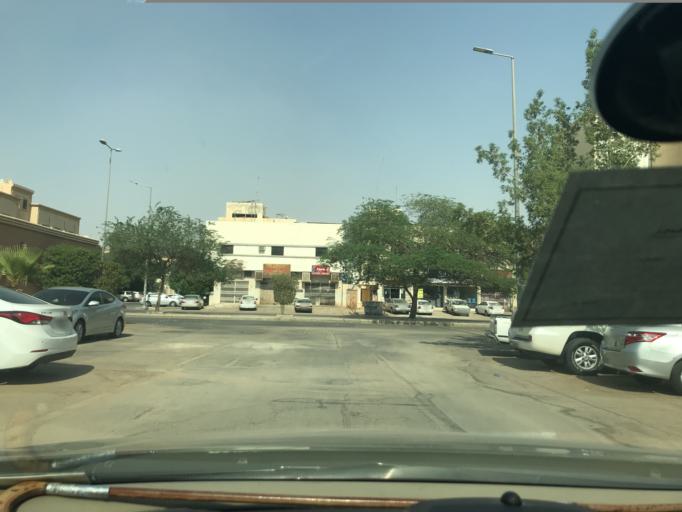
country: SA
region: Ar Riyad
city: Riyadh
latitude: 24.7447
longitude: 46.7639
